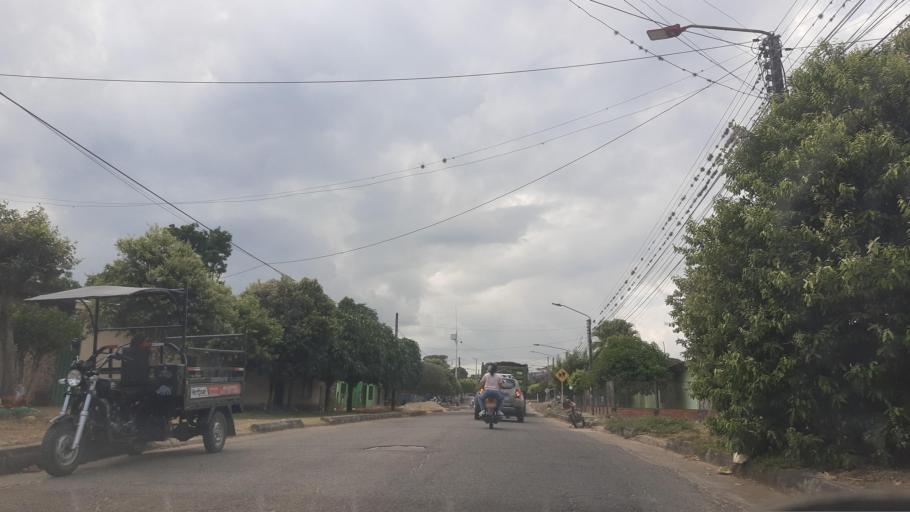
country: CO
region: Casanare
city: Pore
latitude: 5.8832
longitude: -71.8984
